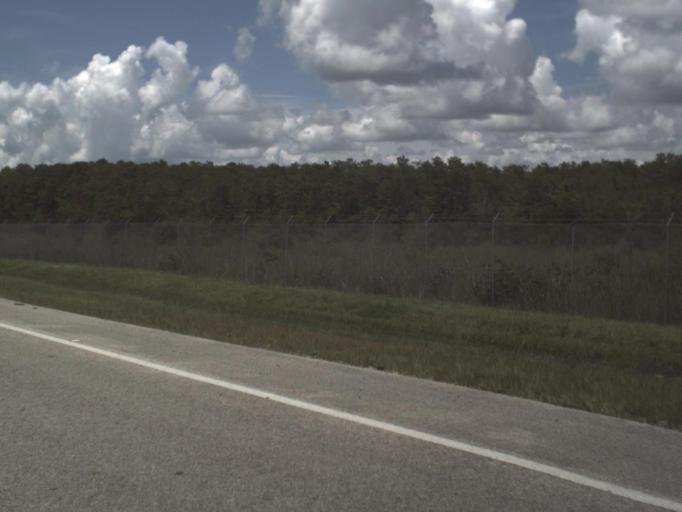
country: US
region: Florida
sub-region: Collier County
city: Immokalee
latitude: 26.1686
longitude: -81.0848
